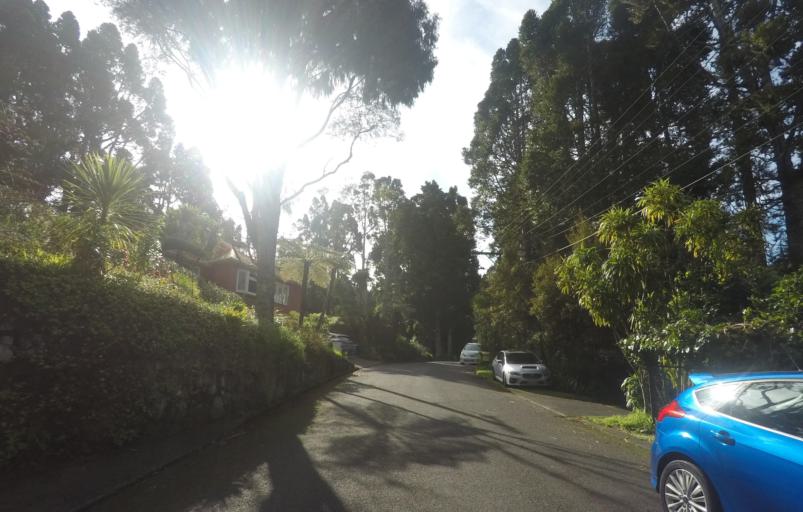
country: NZ
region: Auckland
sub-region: Auckland
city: Titirangi
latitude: -36.9408
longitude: 174.6426
